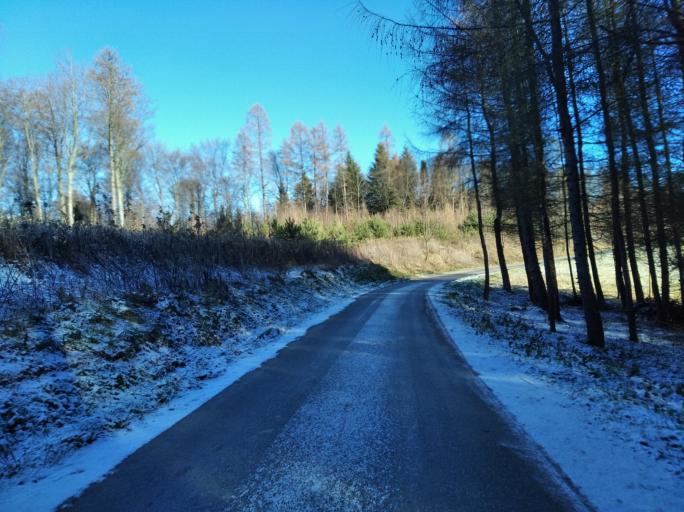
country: PL
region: Subcarpathian Voivodeship
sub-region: Powiat ropczycko-sedziszowski
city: Iwierzyce
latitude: 49.9692
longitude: 21.7282
